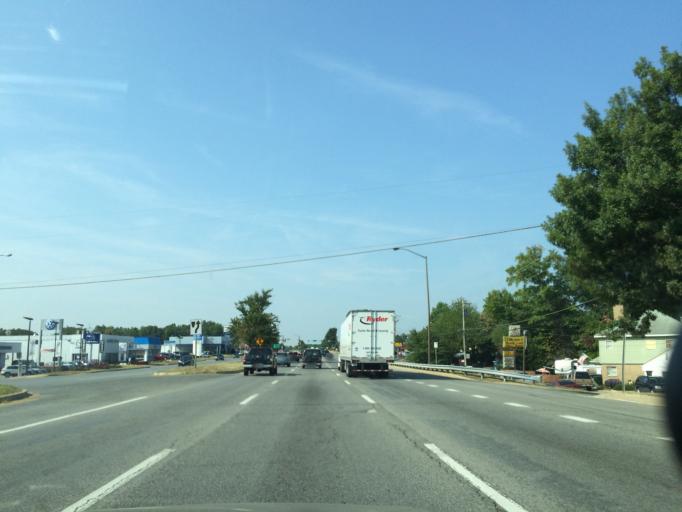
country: US
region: Maryland
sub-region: Charles County
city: Waldorf
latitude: 38.6495
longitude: -76.8856
